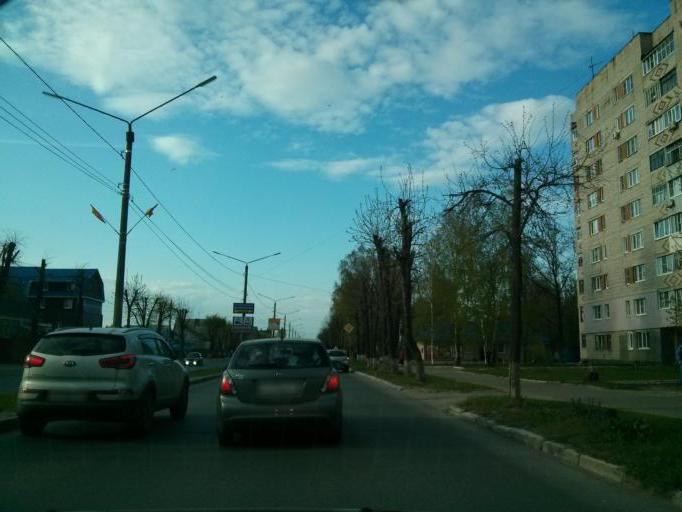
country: RU
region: Vladimir
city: Murom
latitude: 55.5795
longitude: 42.0360
